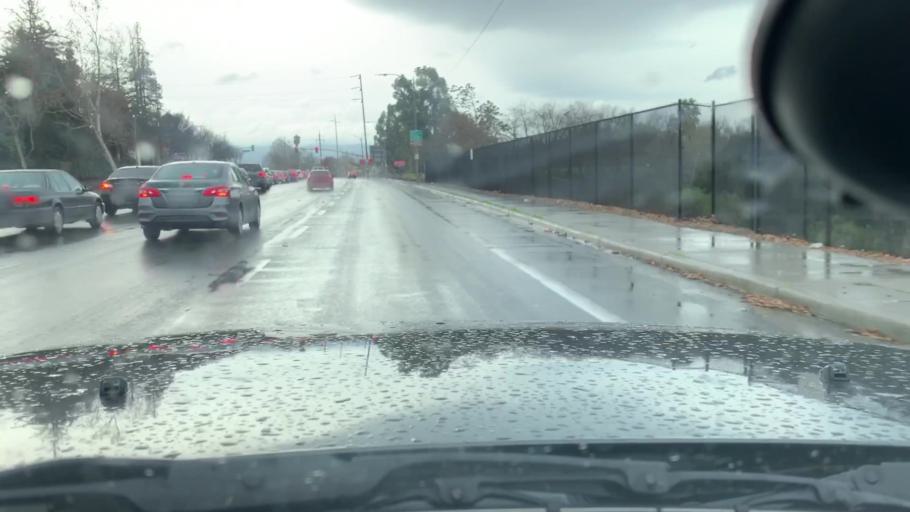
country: US
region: California
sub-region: Santa Clara County
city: San Jose
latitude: 37.3266
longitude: -121.8639
